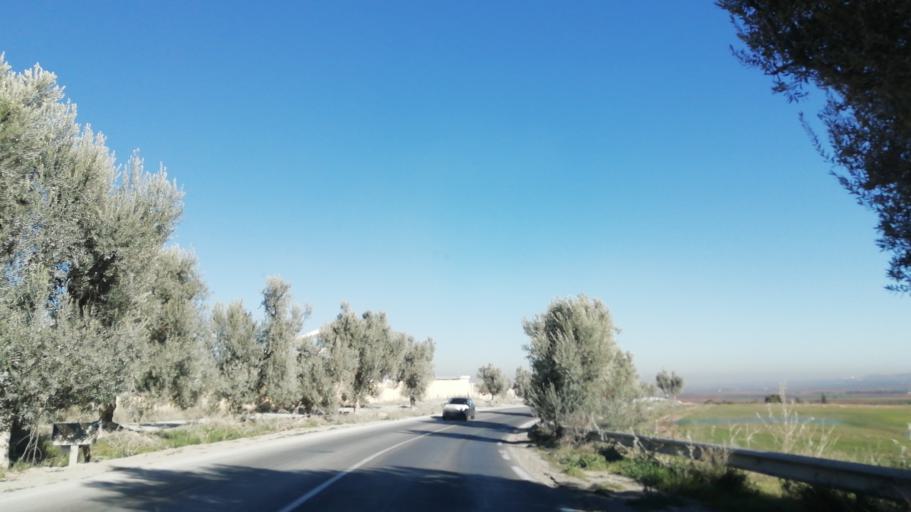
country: DZ
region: Mascara
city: Mascara
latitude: 35.2515
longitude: 0.1221
